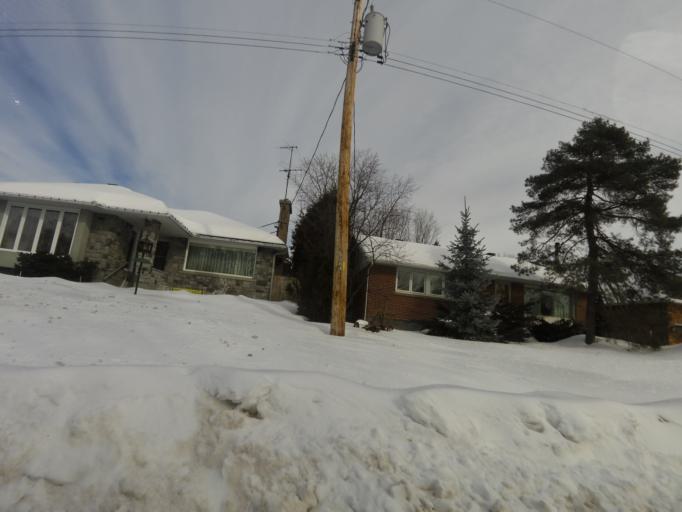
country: CA
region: Ontario
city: Ottawa
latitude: 45.4387
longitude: -75.6081
